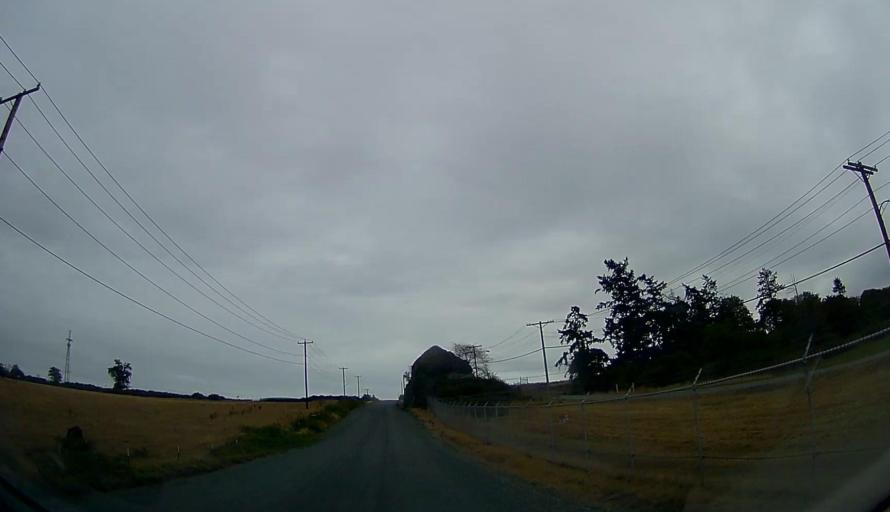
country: US
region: Washington
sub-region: Skagit County
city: Anacortes
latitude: 48.4785
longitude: -122.5692
